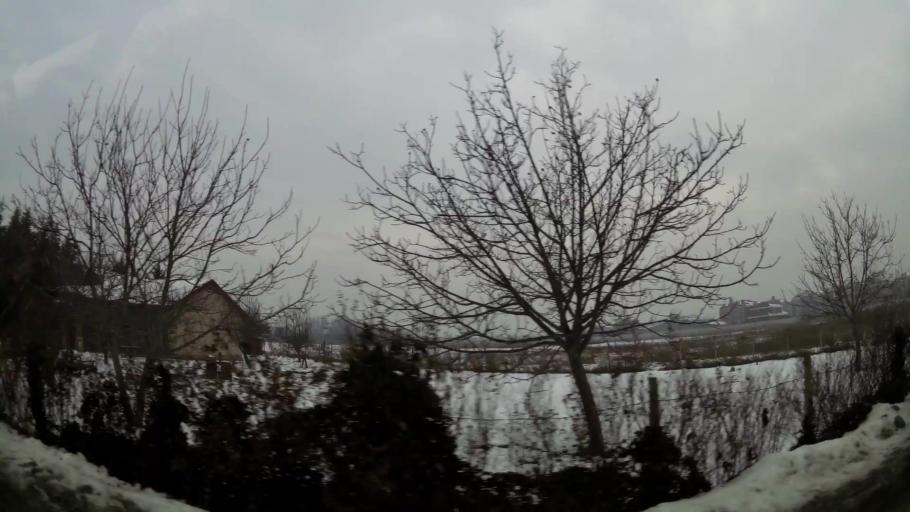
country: MK
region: Cucer-Sandevo
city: Chucher - Sandevo
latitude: 42.0488
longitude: 21.3657
